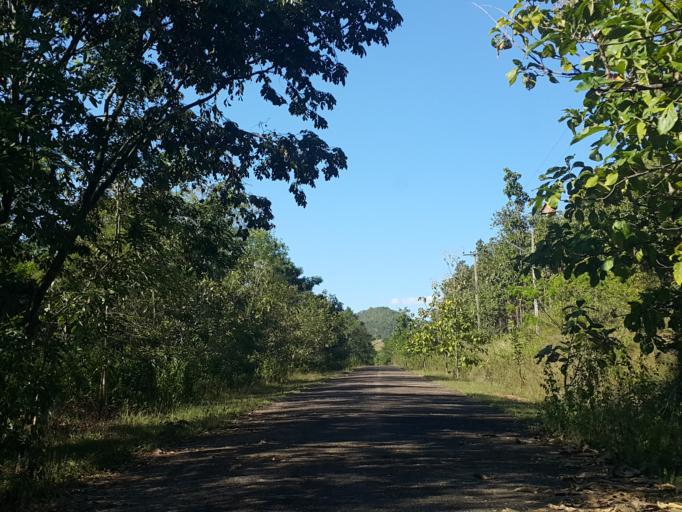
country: TH
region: Chiang Mai
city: San Sai
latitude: 18.9198
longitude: 99.1159
